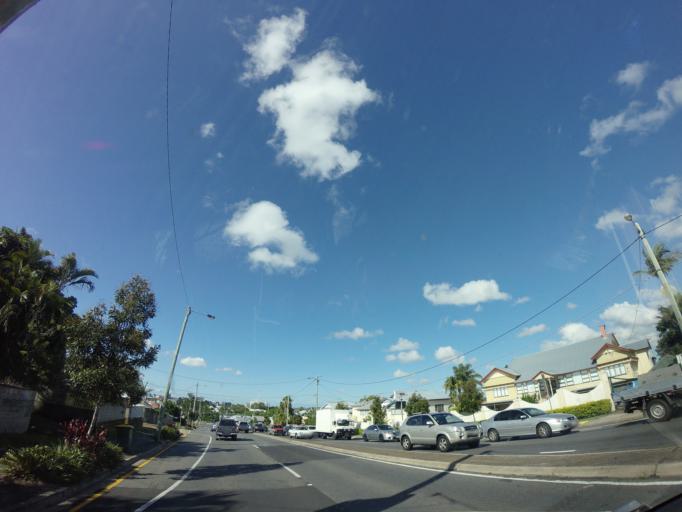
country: AU
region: Queensland
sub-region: Brisbane
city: Annerley
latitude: -27.5076
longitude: 153.0340
